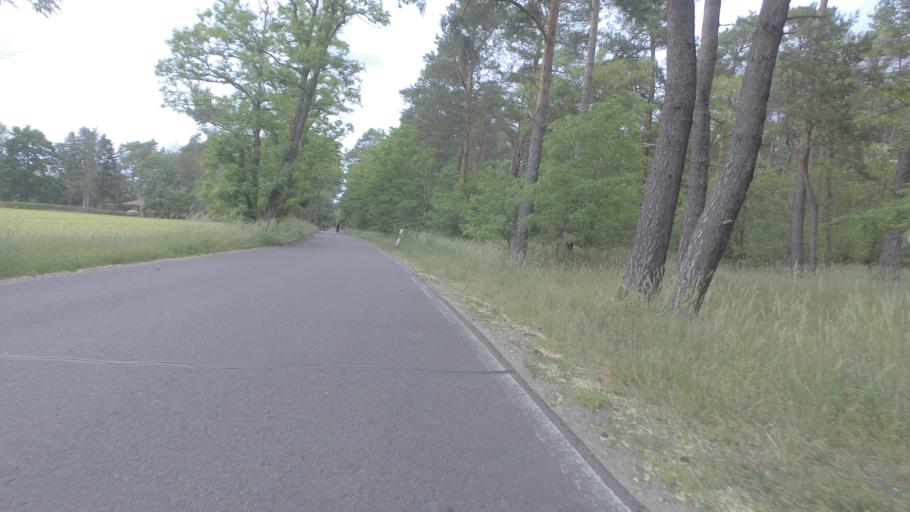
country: DE
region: Brandenburg
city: Bestensee
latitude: 52.2636
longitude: 13.7620
